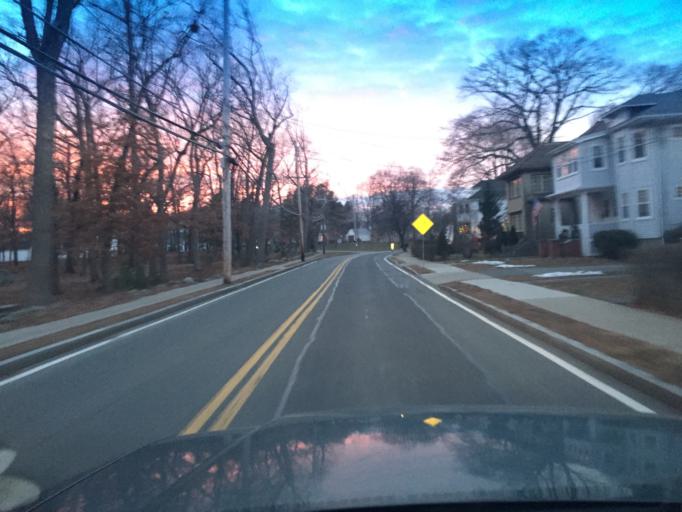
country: US
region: Massachusetts
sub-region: Norfolk County
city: Norwood
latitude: 42.1938
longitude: -71.2107
